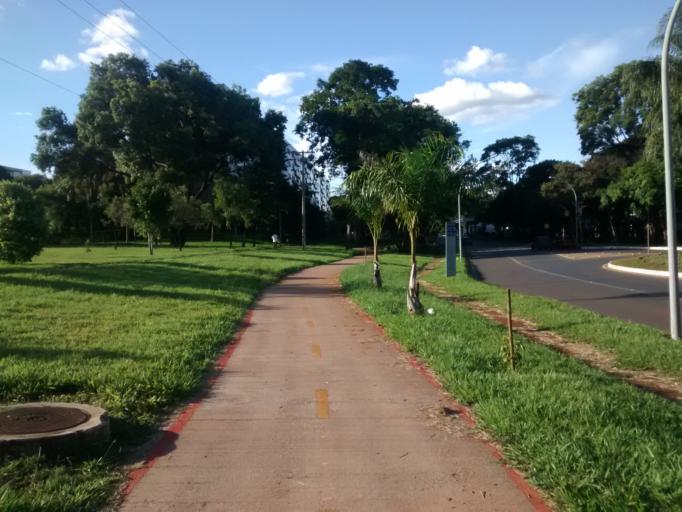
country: BR
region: Federal District
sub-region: Brasilia
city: Brasilia
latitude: -15.7804
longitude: -47.8772
